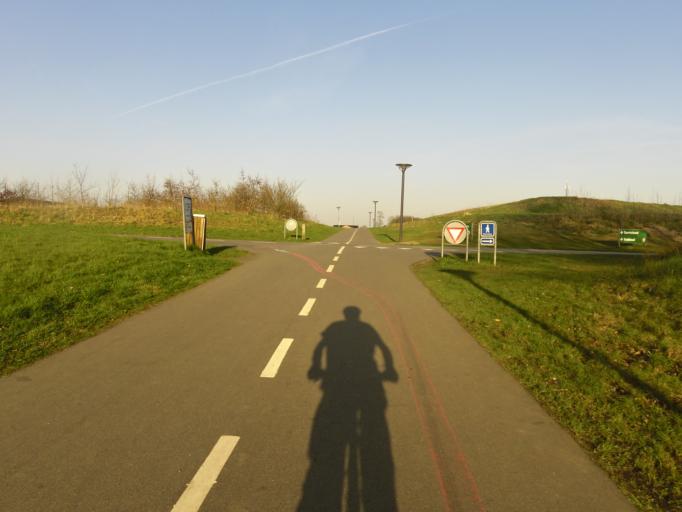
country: DK
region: South Denmark
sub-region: Vejen Kommune
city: Vejen
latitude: 55.4739
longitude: 9.1235
